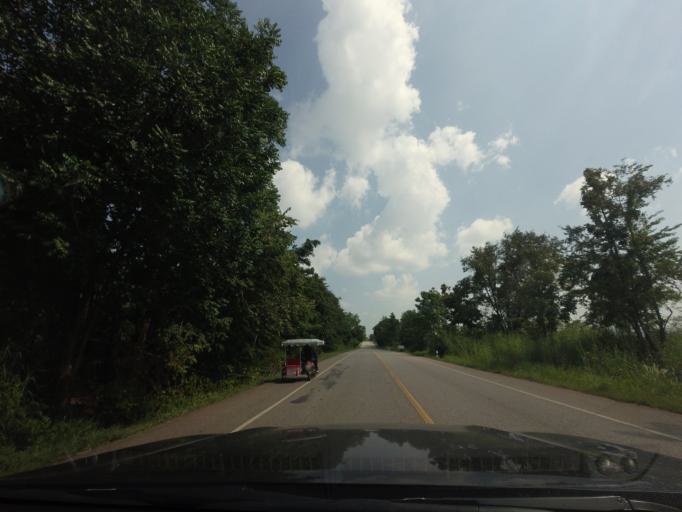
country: TH
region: Phitsanulok
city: Chat Trakan
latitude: 17.2678
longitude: 100.5482
